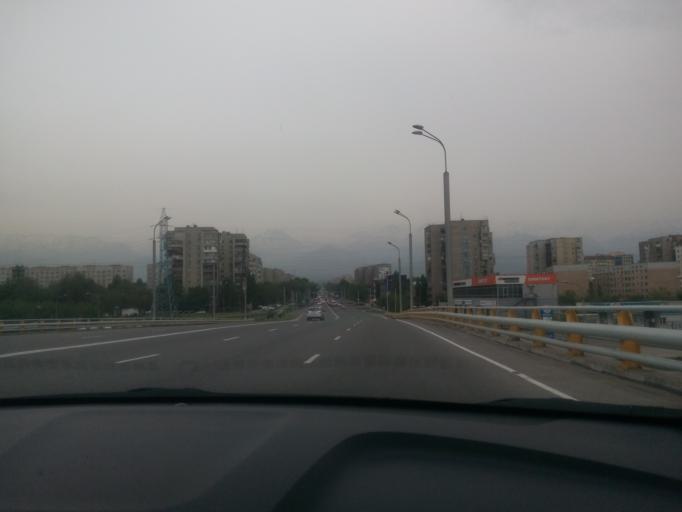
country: KZ
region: Almaty Qalasy
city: Almaty
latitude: 43.2434
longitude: 76.8278
